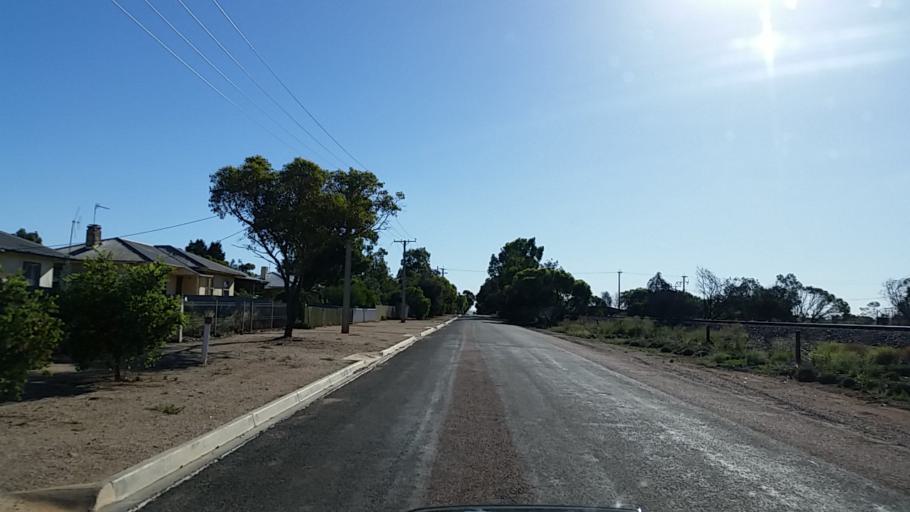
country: AU
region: South Australia
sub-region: Peterborough
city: Peterborough
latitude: -32.9767
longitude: 138.8253
